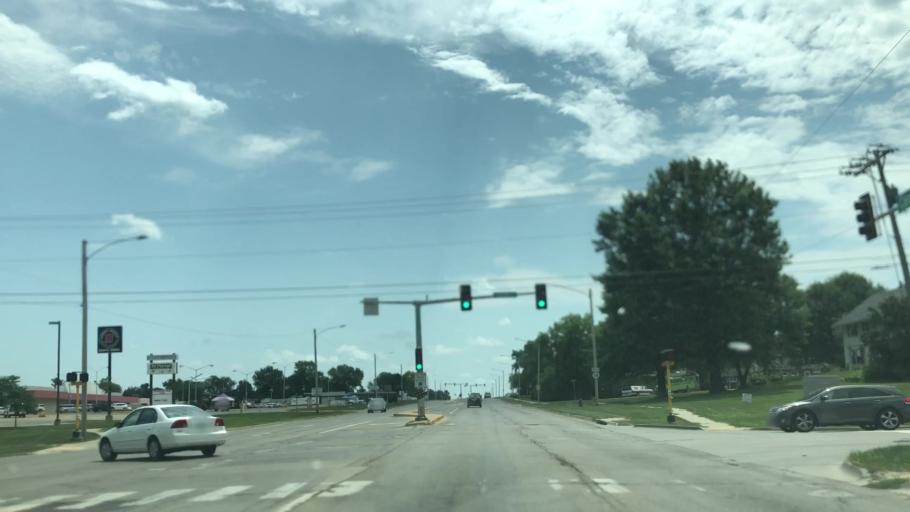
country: US
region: Iowa
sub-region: Marshall County
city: Marshalltown
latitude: 42.0286
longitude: -92.9127
